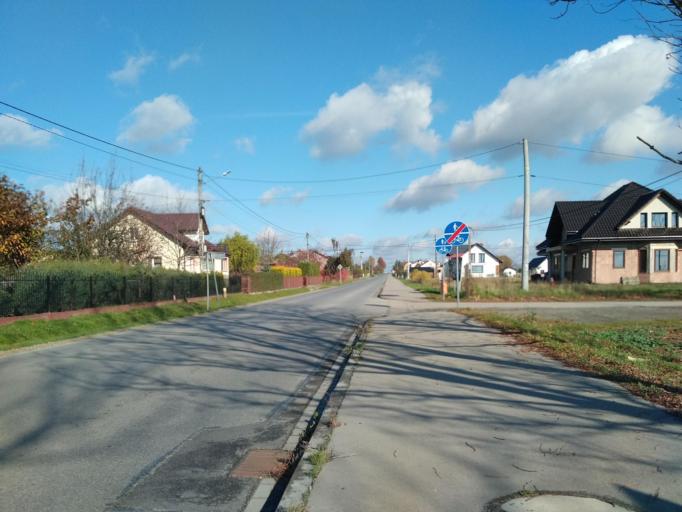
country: PL
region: Subcarpathian Voivodeship
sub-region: Powiat rzeszowski
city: Trzciana
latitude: 50.0997
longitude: 21.8517
